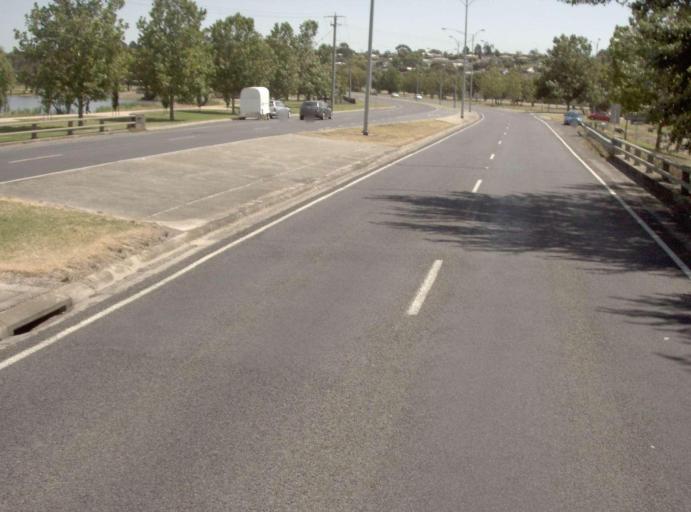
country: AU
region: Victoria
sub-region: Latrobe
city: Morwell
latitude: -38.2364
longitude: 146.4245
